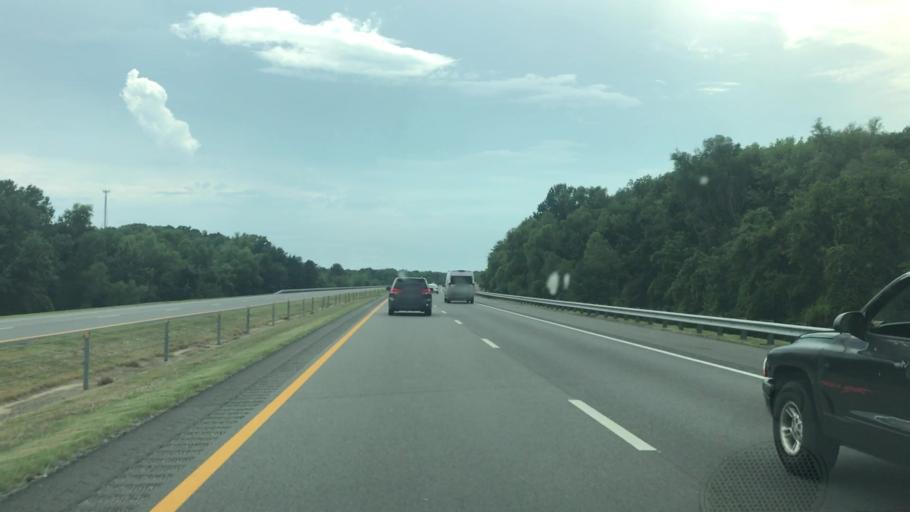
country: US
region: Arkansas
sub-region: Monroe County
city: Brinkley
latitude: 34.8787
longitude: -91.2683
